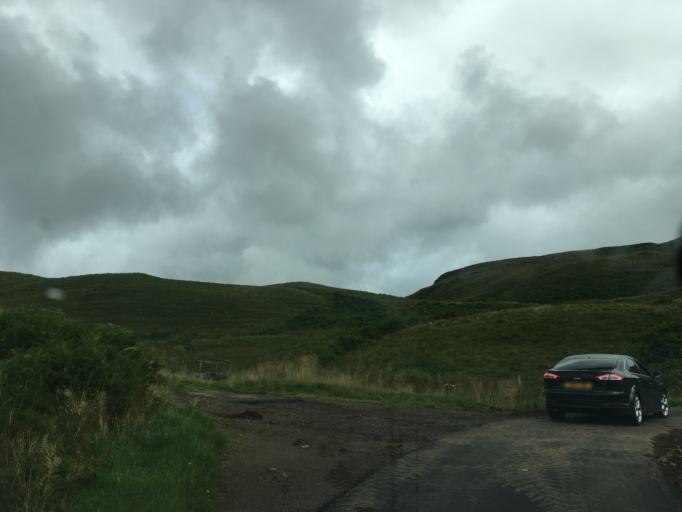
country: GB
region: Scotland
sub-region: Argyll and Bute
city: Oban
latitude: 56.2537
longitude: -5.4491
